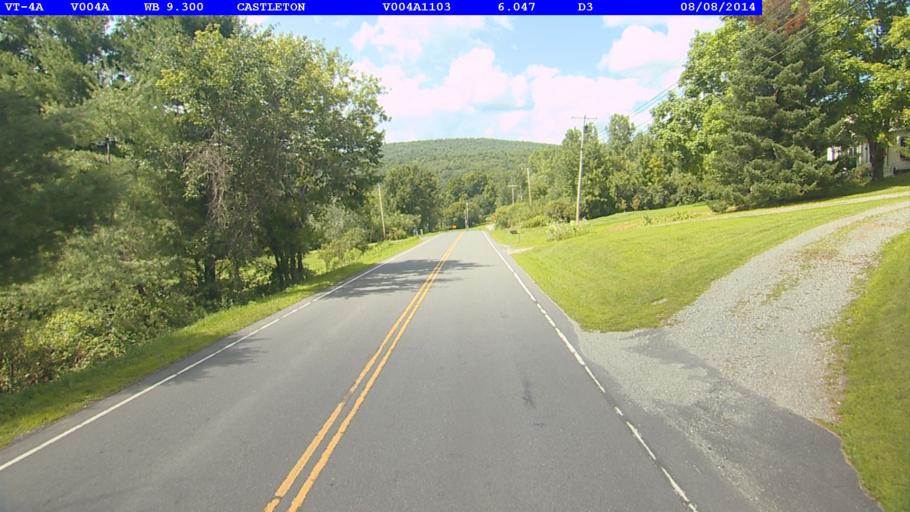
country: US
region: Vermont
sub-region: Rutland County
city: Castleton
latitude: 43.6131
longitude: -73.1285
